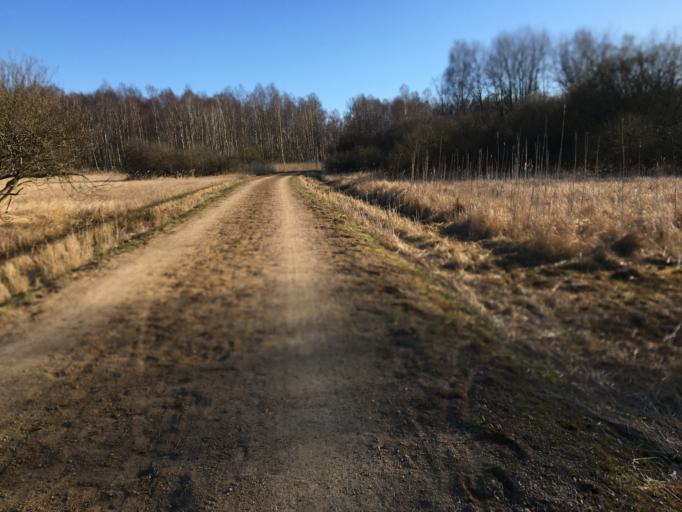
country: DK
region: Capital Region
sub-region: Tarnby Kommune
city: Tarnby
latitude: 55.5917
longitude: 12.5566
